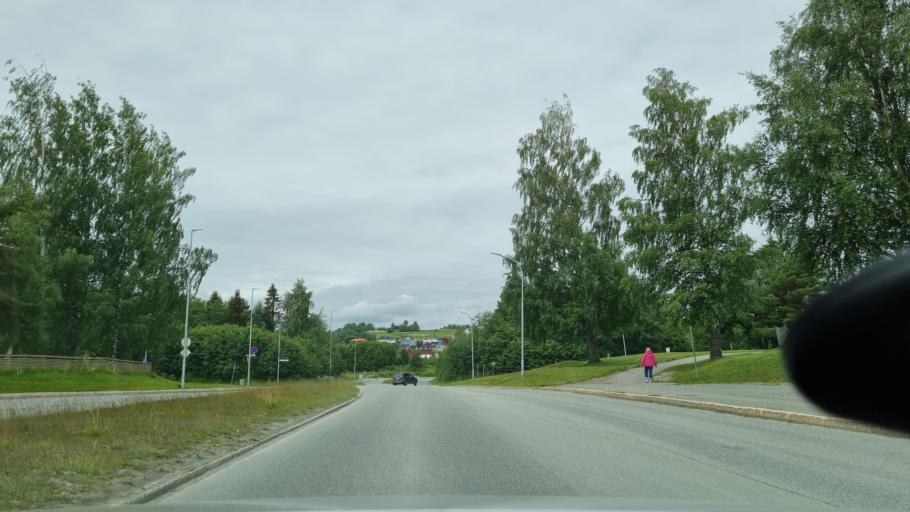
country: NO
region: Sor-Trondelag
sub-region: Melhus
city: Melhus
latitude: 63.3471
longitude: 10.3324
